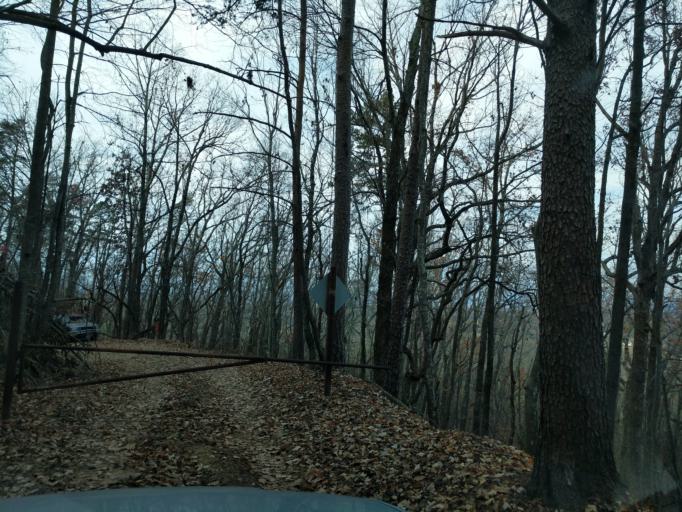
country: US
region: South Carolina
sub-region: Pickens County
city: Pickens
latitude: 34.8339
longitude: -82.8028
